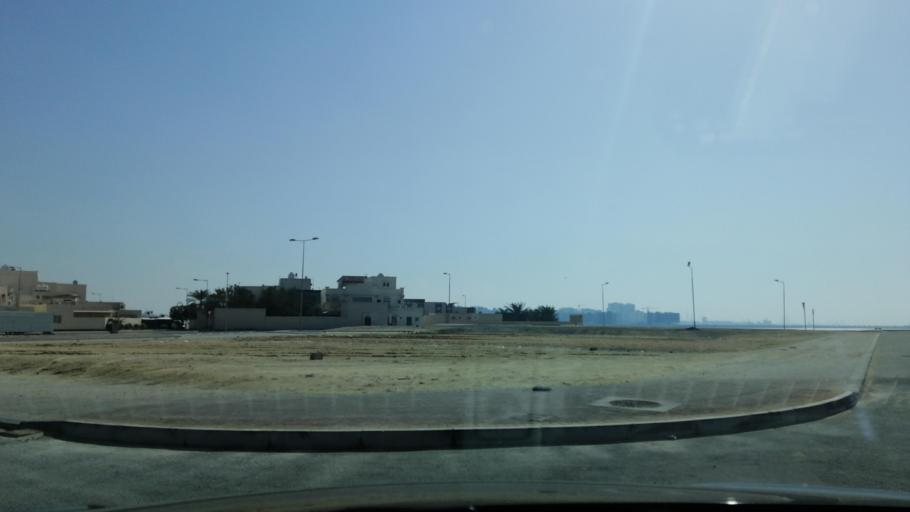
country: BH
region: Muharraq
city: Al Hadd
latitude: 26.2383
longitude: 50.6342
